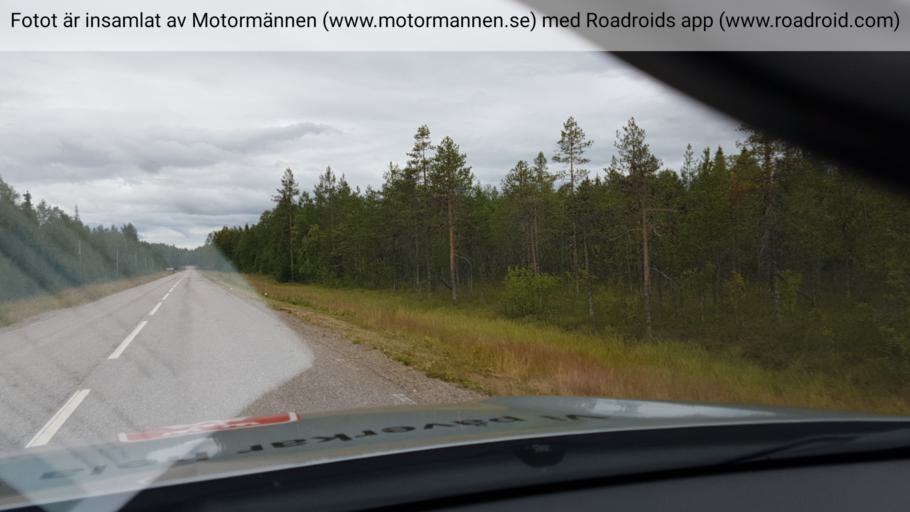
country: SE
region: Norrbotten
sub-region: Overkalix Kommun
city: OEverkalix
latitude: 66.7746
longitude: 22.9014
